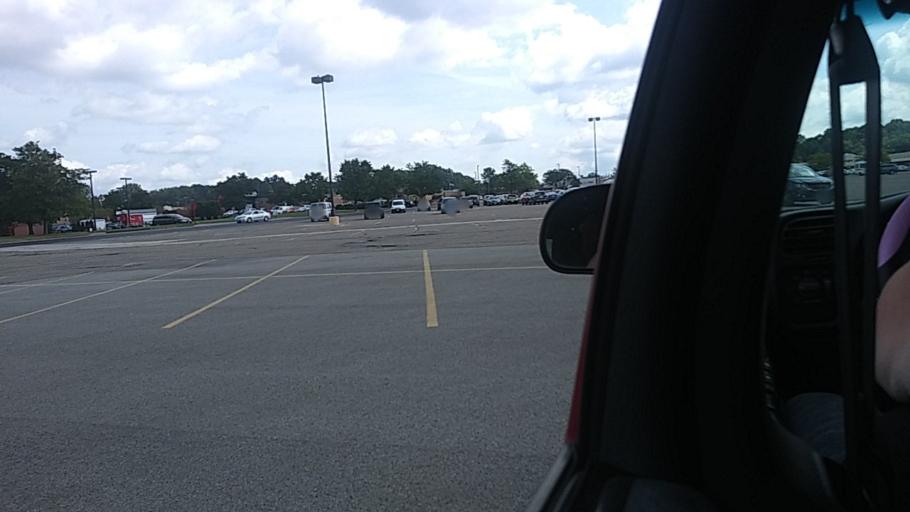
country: US
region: Ohio
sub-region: Summit County
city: Cuyahoga Falls
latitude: 41.1177
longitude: -81.4808
